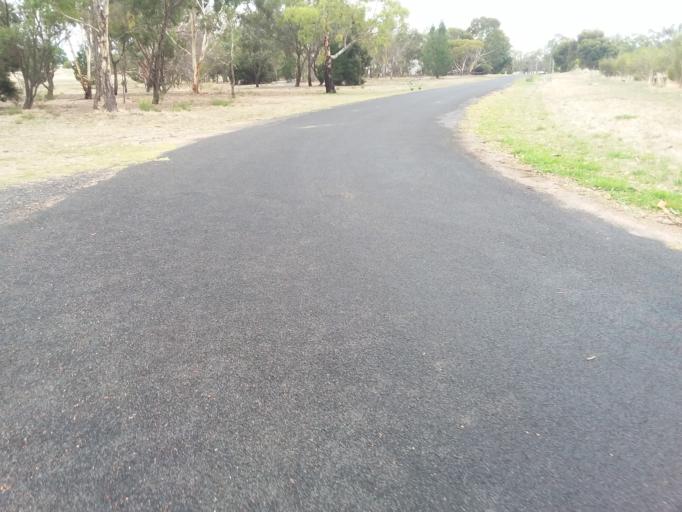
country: AU
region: Victoria
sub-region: Horsham
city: Horsham
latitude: -36.7418
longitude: 141.9359
